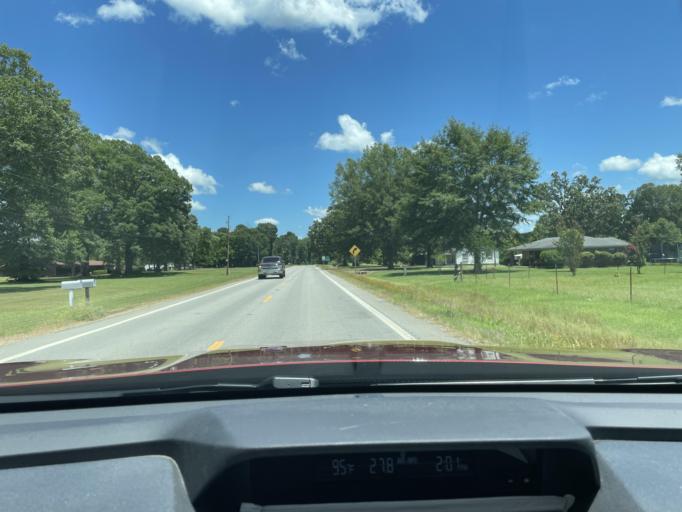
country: US
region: Arkansas
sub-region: Drew County
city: Monticello
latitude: 33.6044
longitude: -91.7292
